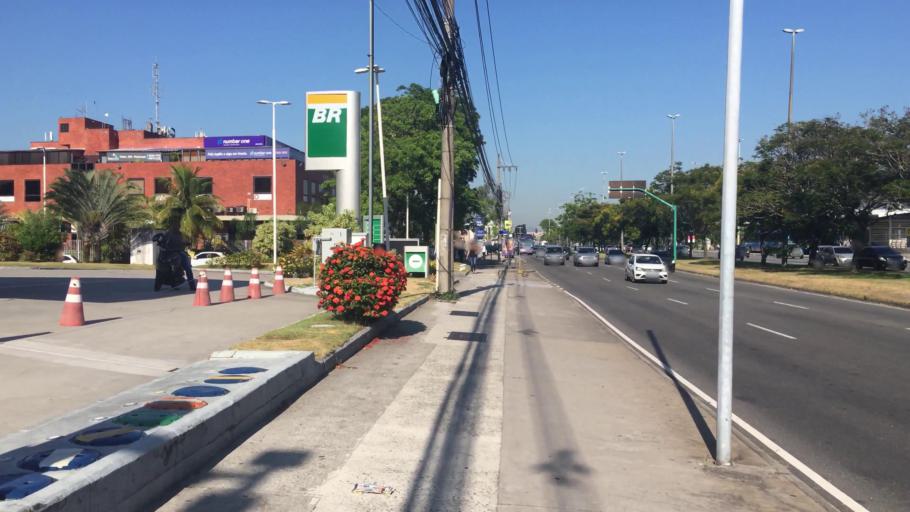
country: BR
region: Rio de Janeiro
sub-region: Rio De Janeiro
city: Rio de Janeiro
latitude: -23.0005
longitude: -43.3515
